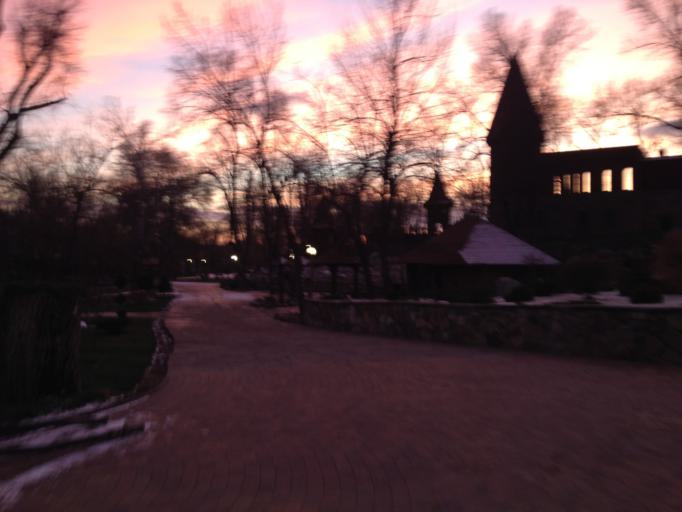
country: RU
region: Rostov
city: Staraya Stanitsa
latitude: 48.3529
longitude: 40.2967
